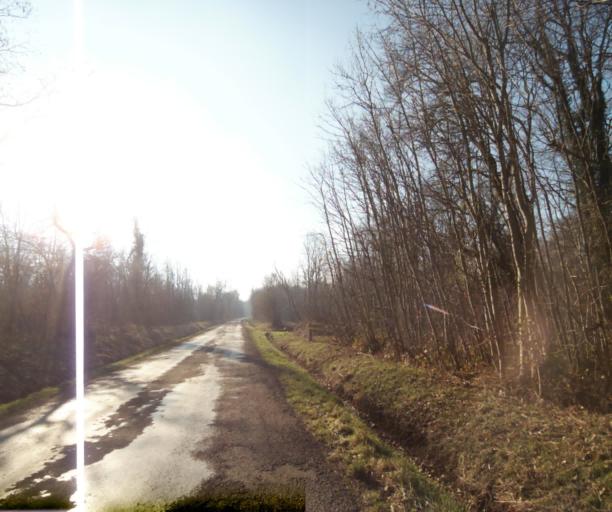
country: FR
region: Champagne-Ardenne
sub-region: Departement de la Haute-Marne
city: Wassy
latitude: 48.5139
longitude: 4.9686
